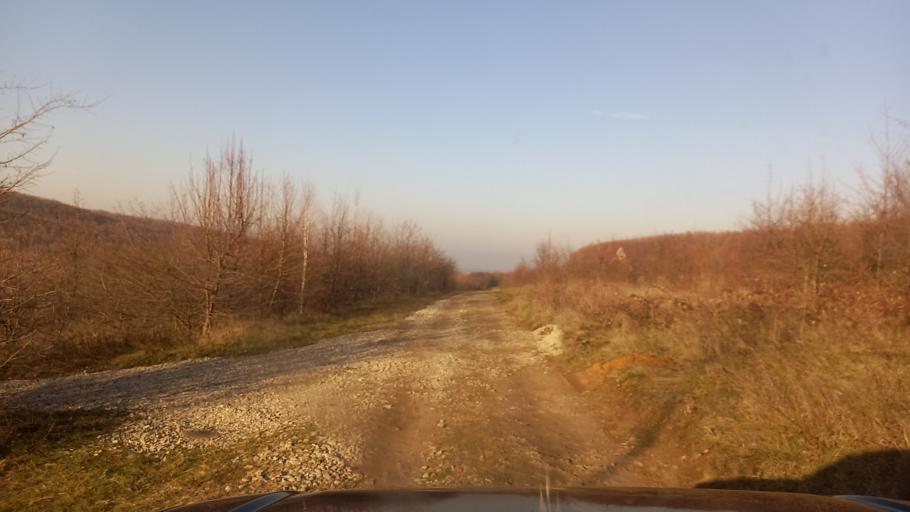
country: RU
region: Krasnodarskiy
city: Il'skiy
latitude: 44.8145
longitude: 38.5944
